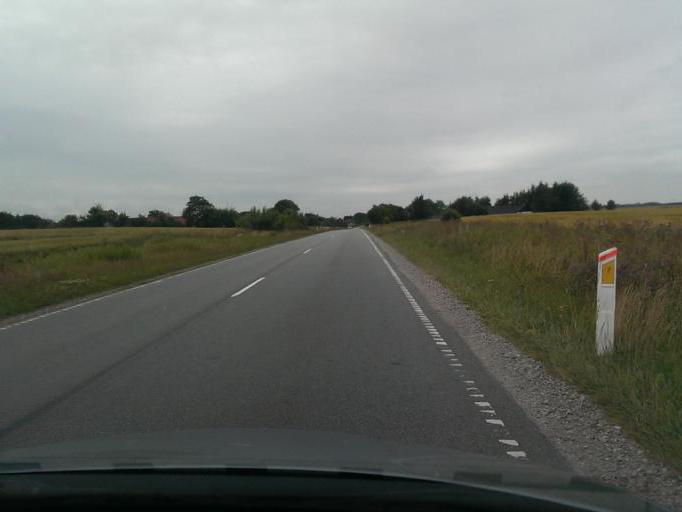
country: DK
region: North Denmark
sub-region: Hjorring Kommune
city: Vra
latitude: 57.3564
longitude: 9.9225
